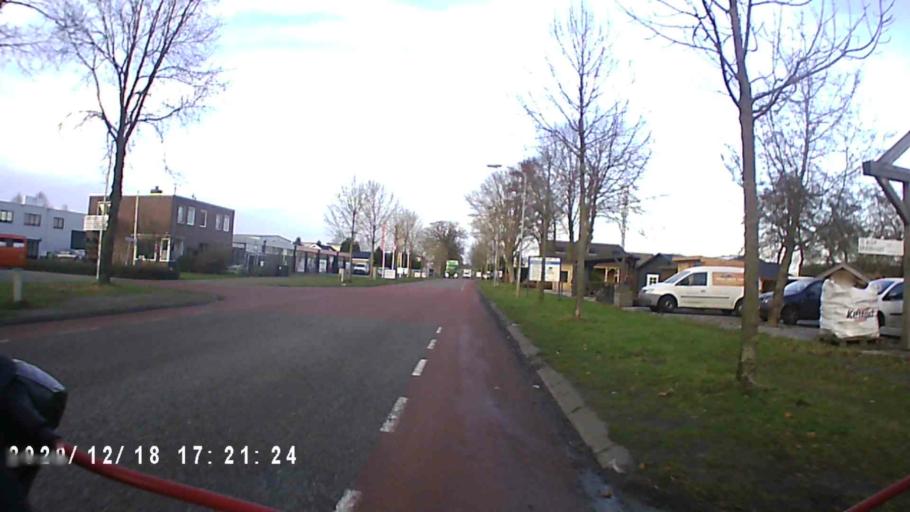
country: NL
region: Drenthe
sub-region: Gemeente Tynaarlo
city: Tynaarlo
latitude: 53.0811
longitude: 6.5982
